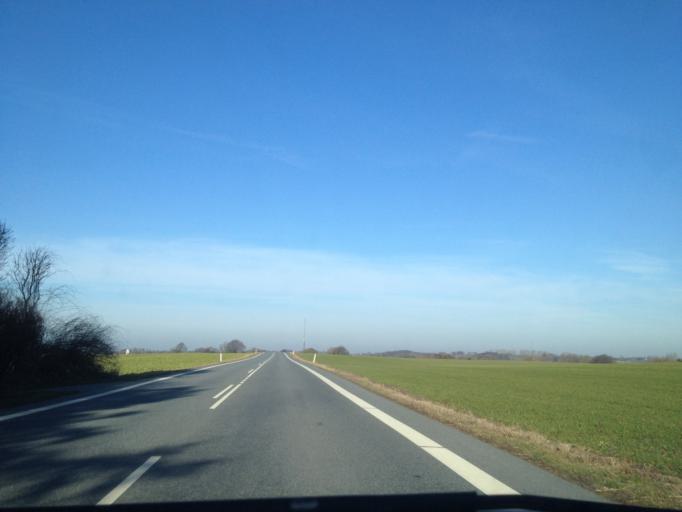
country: DK
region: South Denmark
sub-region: Kerteminde Kommune
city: Kerteminde
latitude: 55.4860
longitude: 10.6591
